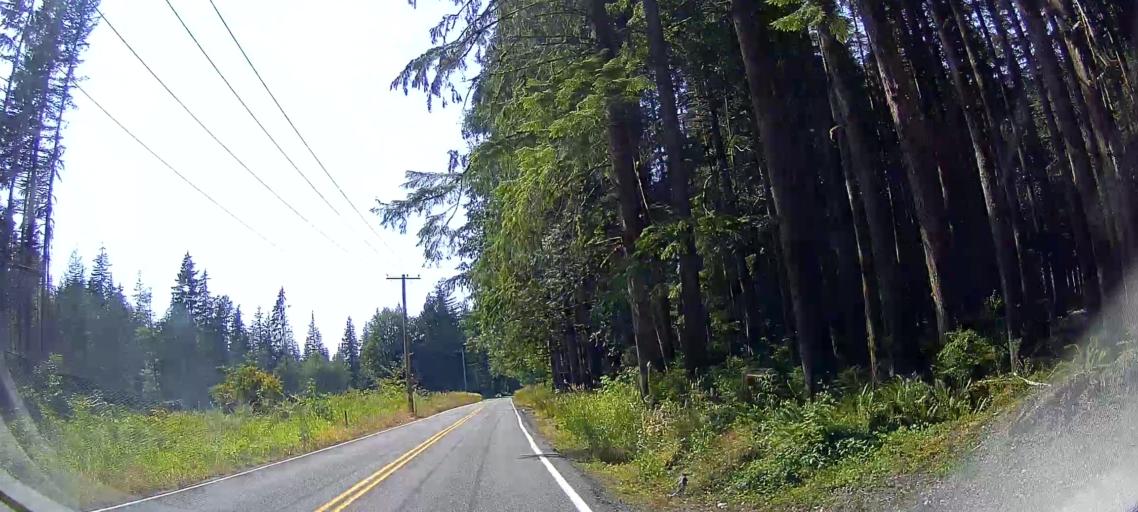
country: US
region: Washington
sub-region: Snohomish County
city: Bryant
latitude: 48.3431
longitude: -122.0910
